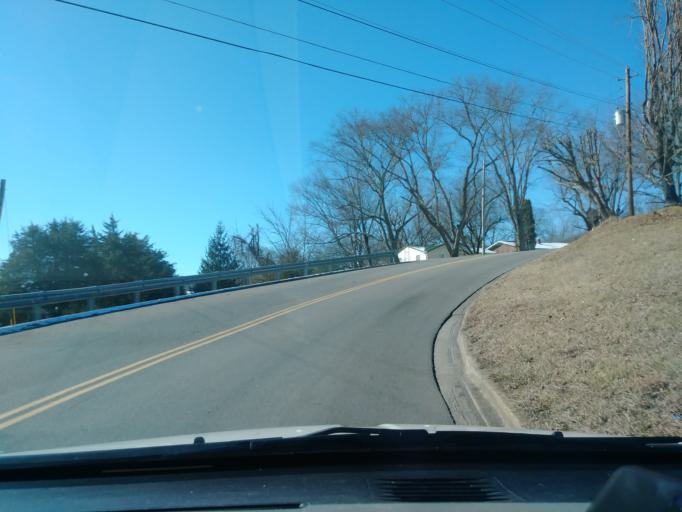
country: US
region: Tennessee
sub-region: Greene County
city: Greeneville
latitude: 36.1511
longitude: -82.8360
